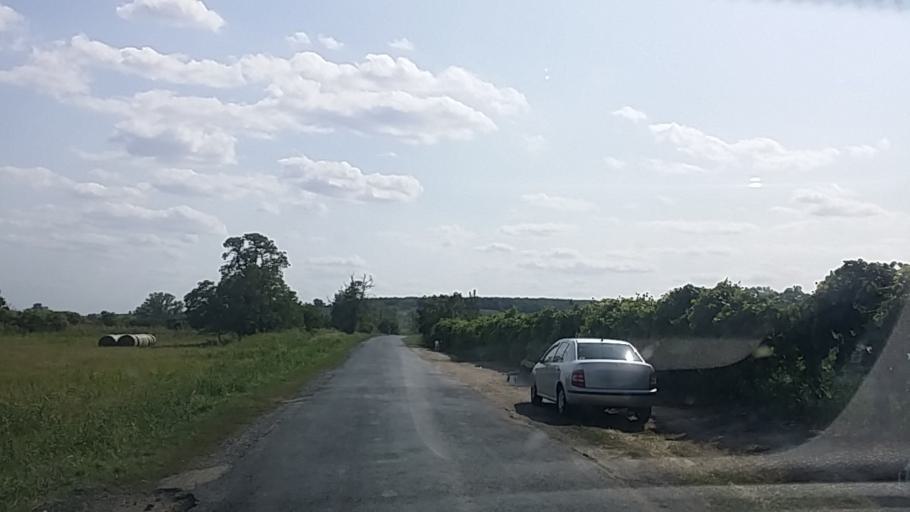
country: HU
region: Gyor-Moson-Sopron
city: Fertorakos
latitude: 47.6885
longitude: 16.6641
